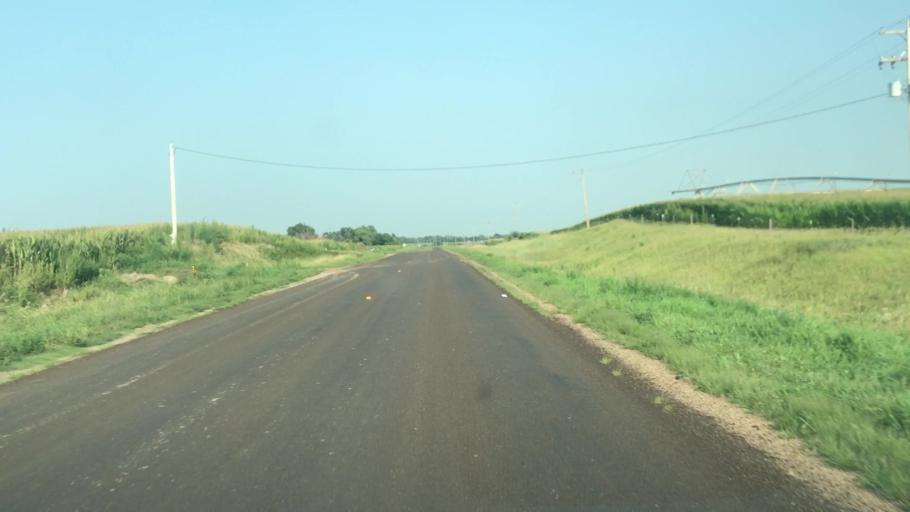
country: US
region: Nebraska
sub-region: Buffalo County
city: Ravenna
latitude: 41.0757
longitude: -98.7446
